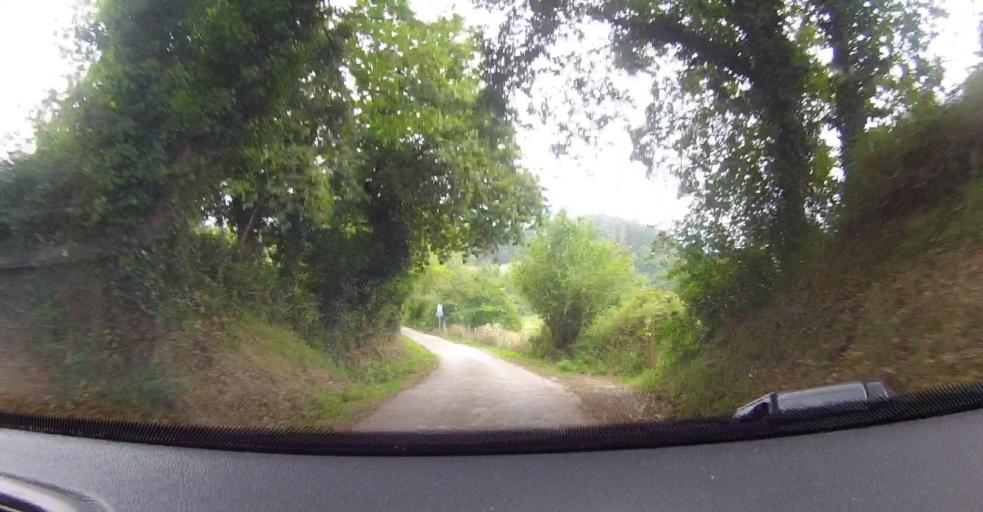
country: ES
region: Basque Country
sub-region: Bizkaia
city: Sopuerta
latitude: 43.2579
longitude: -3.1356
